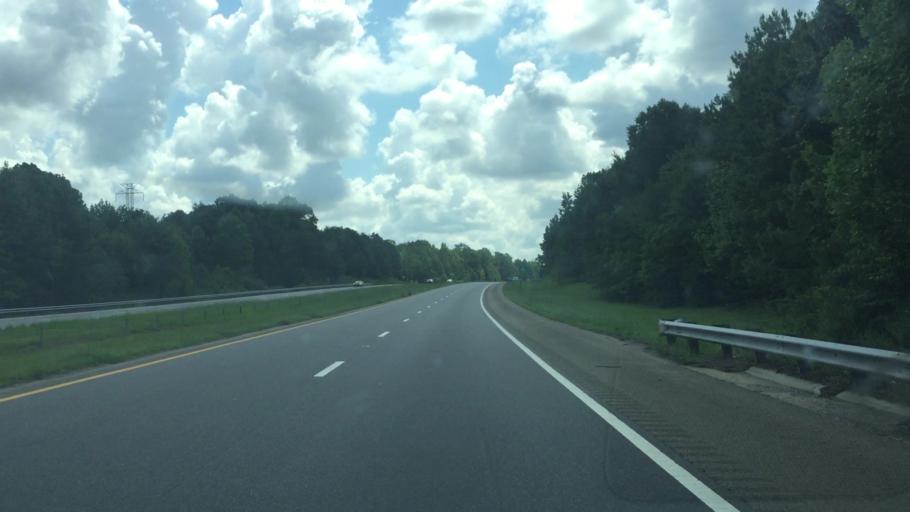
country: US
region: North Carolina
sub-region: Richmond County
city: Cordova
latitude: 34.9176
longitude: -79.8017
